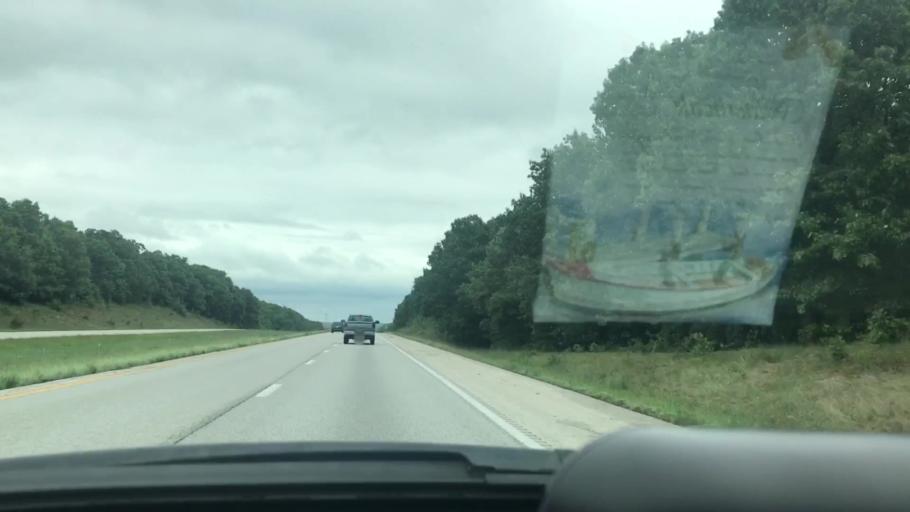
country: US
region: Missouri
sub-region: Lawrence County
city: Mount Vernon
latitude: 37.1446
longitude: -93.7132
